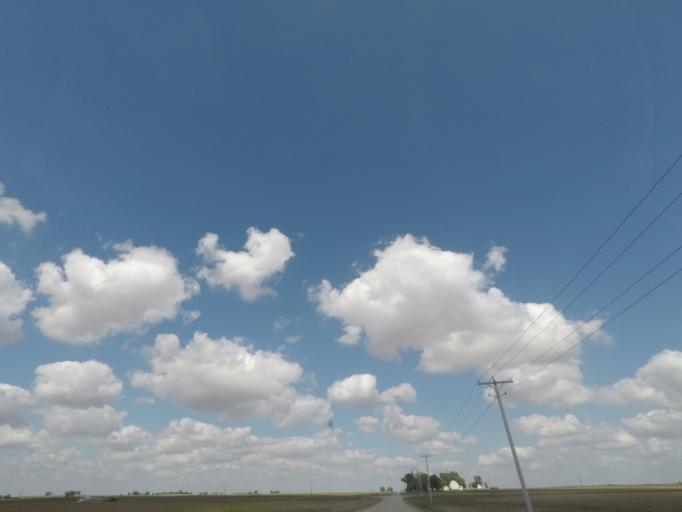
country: US
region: Iowa
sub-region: Story County
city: Nevada
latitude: 42.0763
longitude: -93.3864
